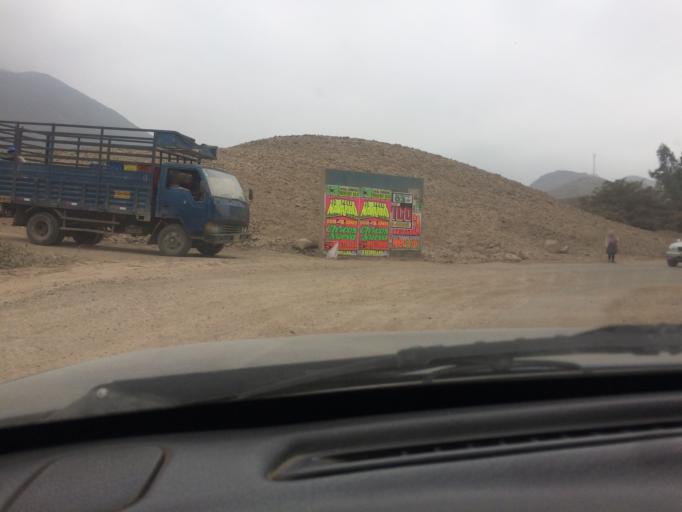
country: PE
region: Lima
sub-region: Lima
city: Cieneguilla
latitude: -12.1770
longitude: -76.8638
